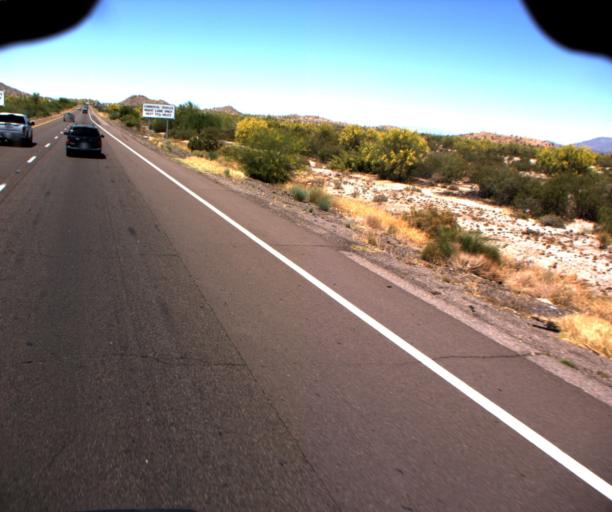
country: US
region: Arizona
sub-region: Pinal County
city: Sacaton
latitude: 33.0085
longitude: -111.7571
